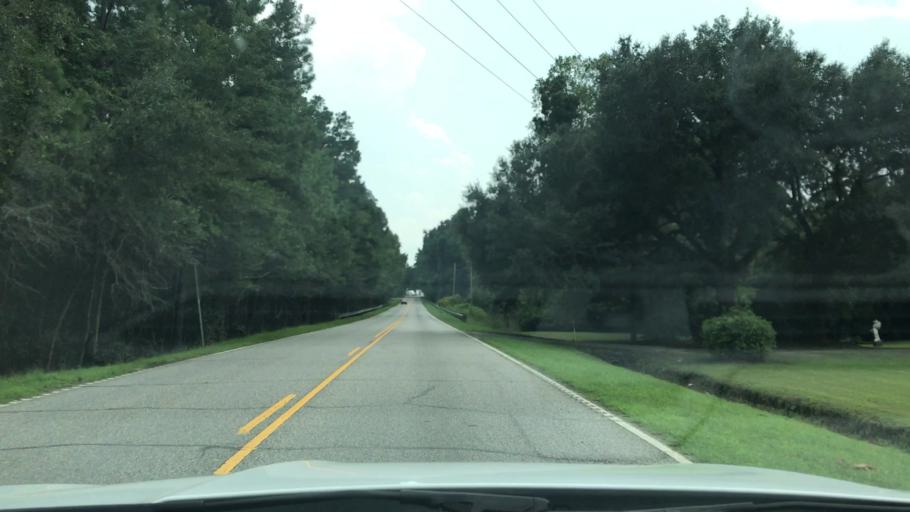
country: US
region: South Carolina
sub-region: Georgetown County
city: Murrells Inlet
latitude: 33.5601
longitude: -79.2147
